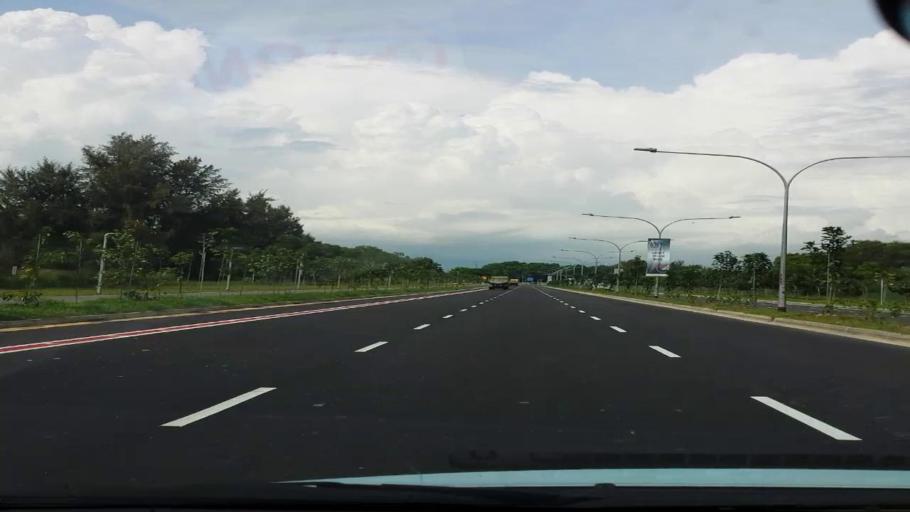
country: SG
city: Singapore
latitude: 1.3222
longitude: 104.0174
